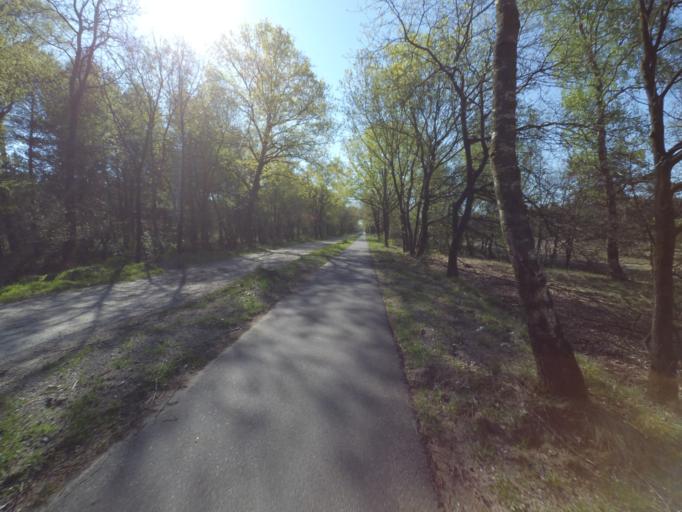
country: NL
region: Gelderland
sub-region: Gemeente Apeldoorn
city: Uddel
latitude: 52.1902
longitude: 5.8053
